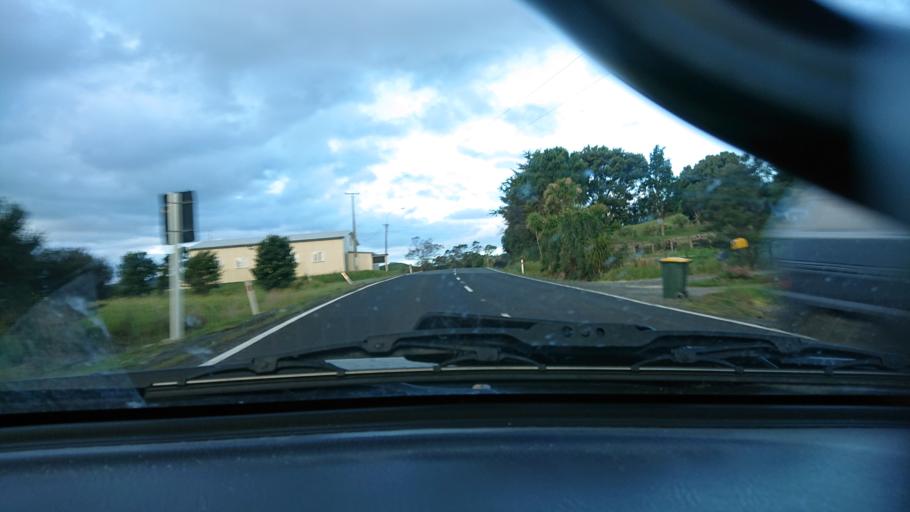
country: NZ
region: Auckland
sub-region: Auckland
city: Parakai
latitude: -36.4750
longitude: 174.4480
